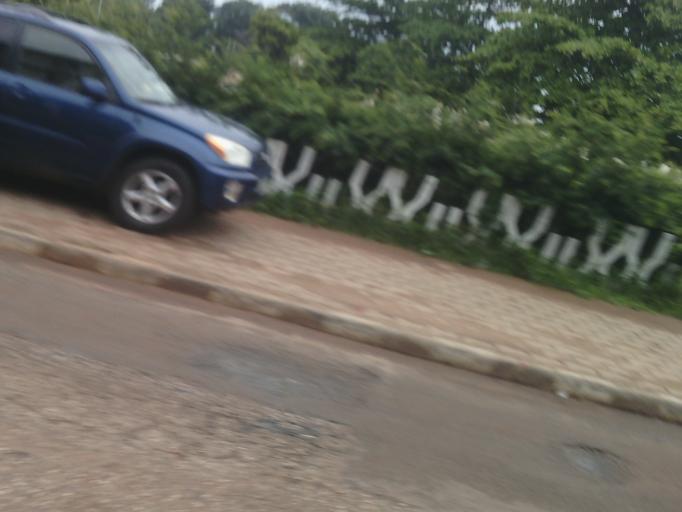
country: BJ
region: Queme
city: Porto-Novo
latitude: 6.4740
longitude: 2.6176
